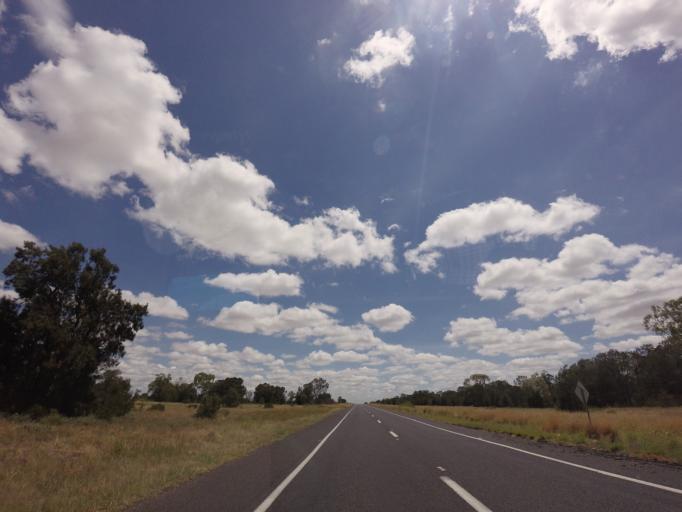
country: AU
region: New South Wales
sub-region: Moree Plains
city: Moree
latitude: -29.1321
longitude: 150.0239
